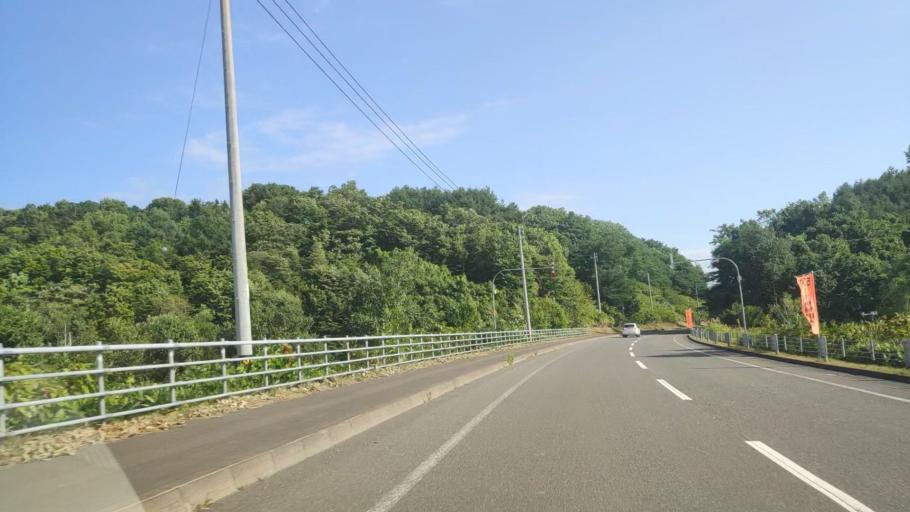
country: JP
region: Hokkaido
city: Ishikari
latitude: 43.6347
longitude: 141.3623
